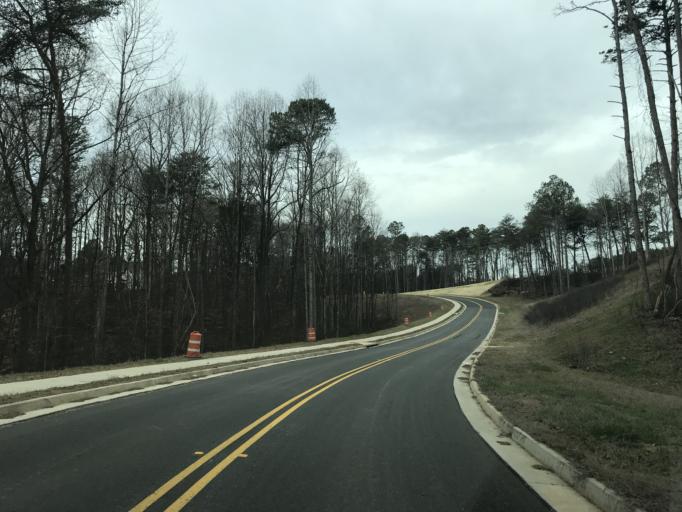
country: US
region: Georgia
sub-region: Forsyth County
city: Cumming
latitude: 34.2285
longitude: -84.0973
